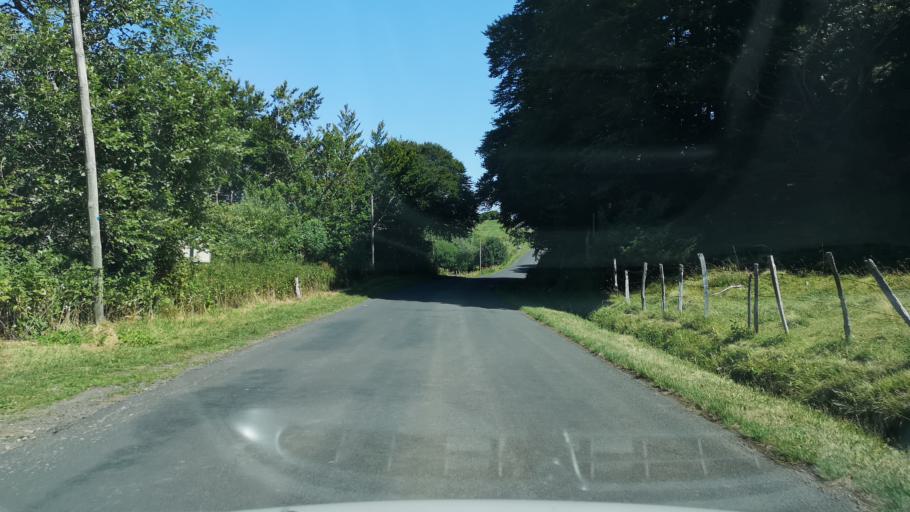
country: FR
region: Auvergne
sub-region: Departement du Puy-de-Dome
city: Mont-Dore
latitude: 45.5445
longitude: 2.8700
